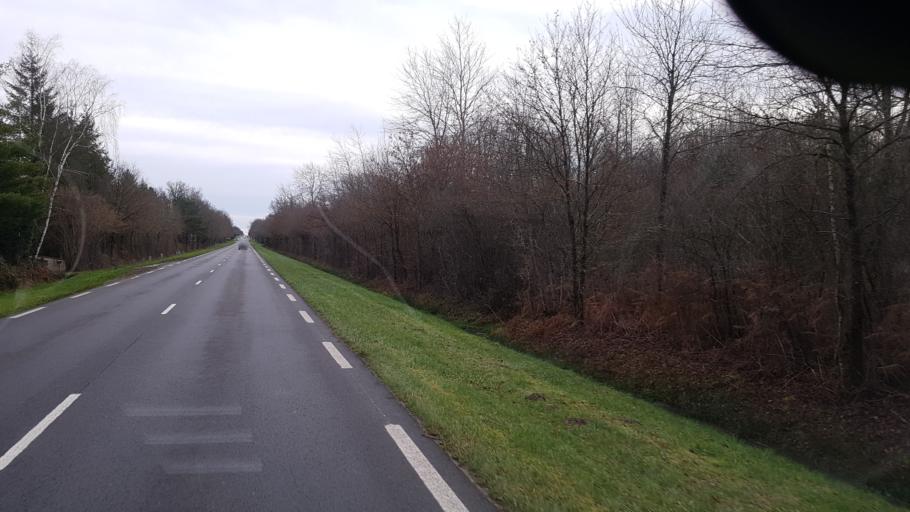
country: FR
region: Centre
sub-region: Departement du Loiret
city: Menestreau-en-Villette
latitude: 47.6593
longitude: 1.9820
